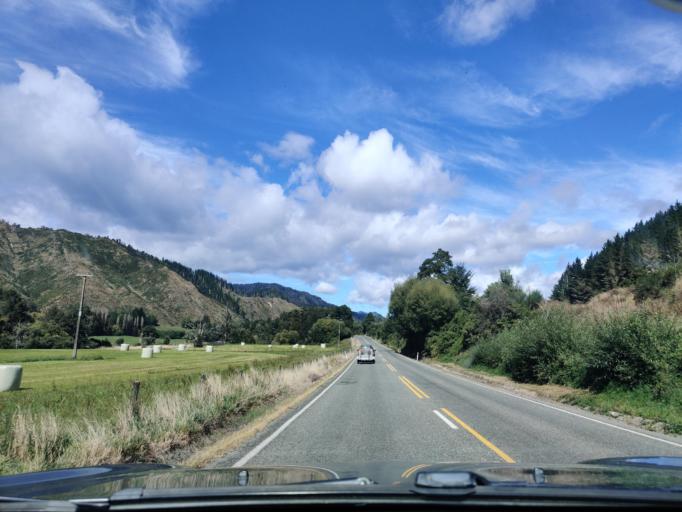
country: NZ
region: Tasman
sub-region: Tasman District
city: Wakefield
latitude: -41.7187
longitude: 172.4086
